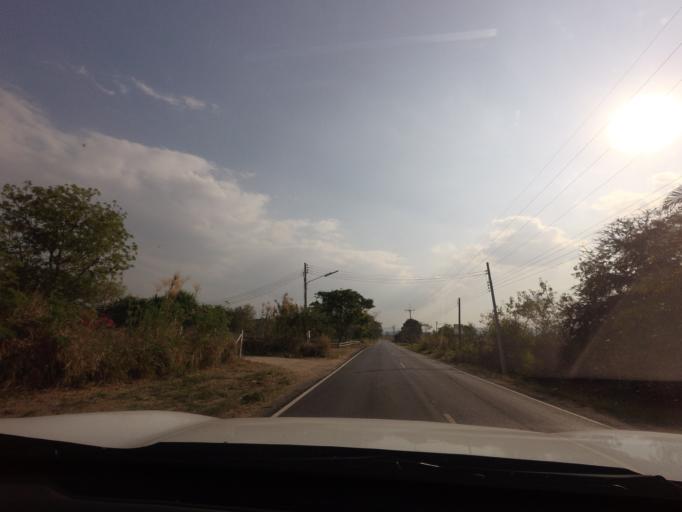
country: TH
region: Nakhon Ratchasima
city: Pak Chong
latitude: 14.6234
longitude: 101.4553
